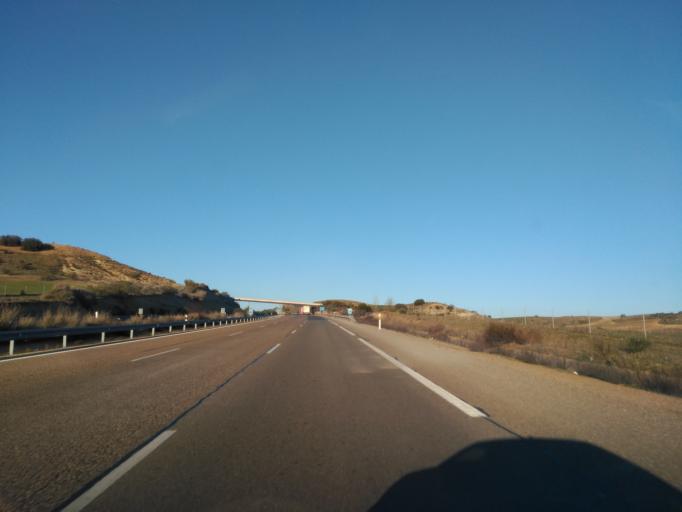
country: ES
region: Castille and Leon
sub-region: Provincia de Zamora
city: Castrillo de la Guarena
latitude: 41.2355
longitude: -5.3069
